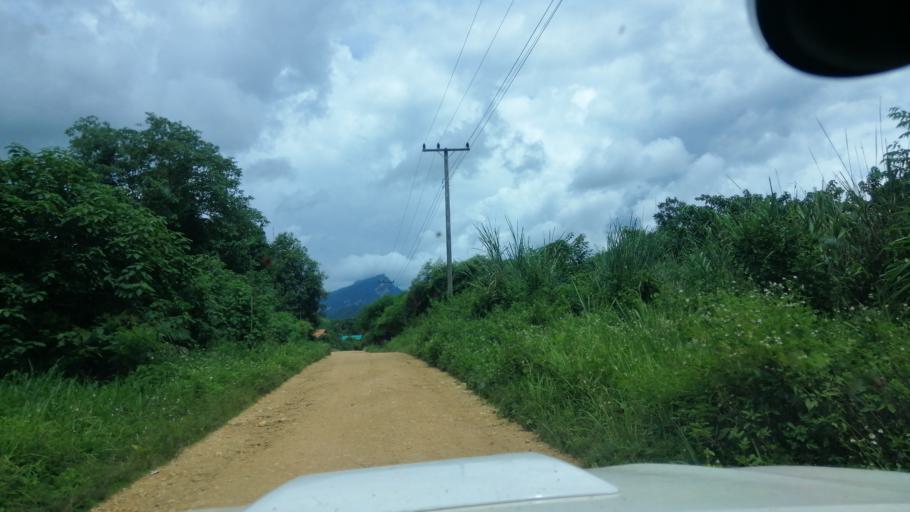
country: TH
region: Phayao
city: Phu Sang
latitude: 19.7080
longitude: 100.4899
